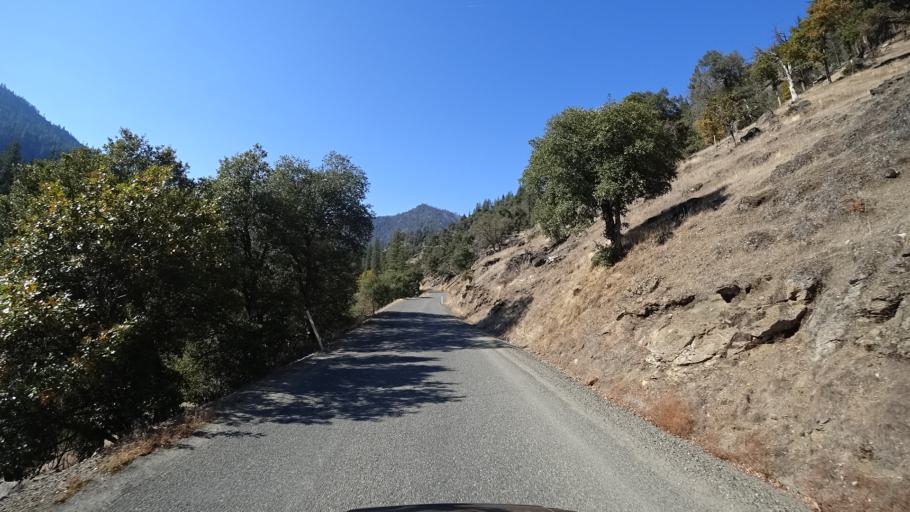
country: US
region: California
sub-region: Siskiyou County
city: Happy Camp
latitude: 41.6879
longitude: -123.0850
